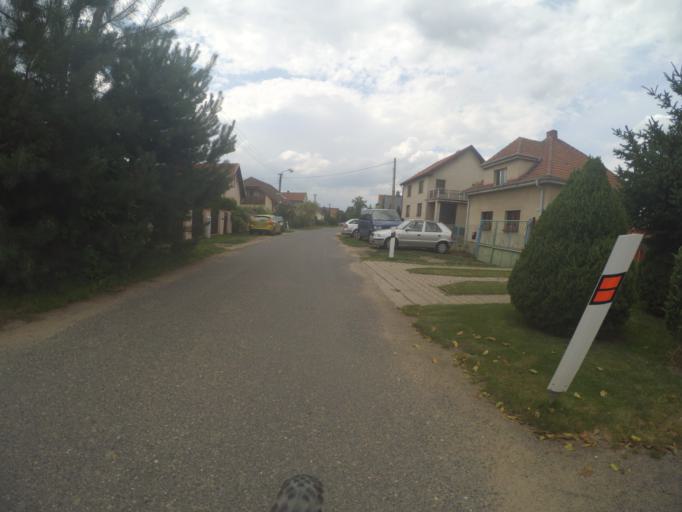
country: CZ
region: Central Bohemia
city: Libis
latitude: 50.2911
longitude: 14.4798
